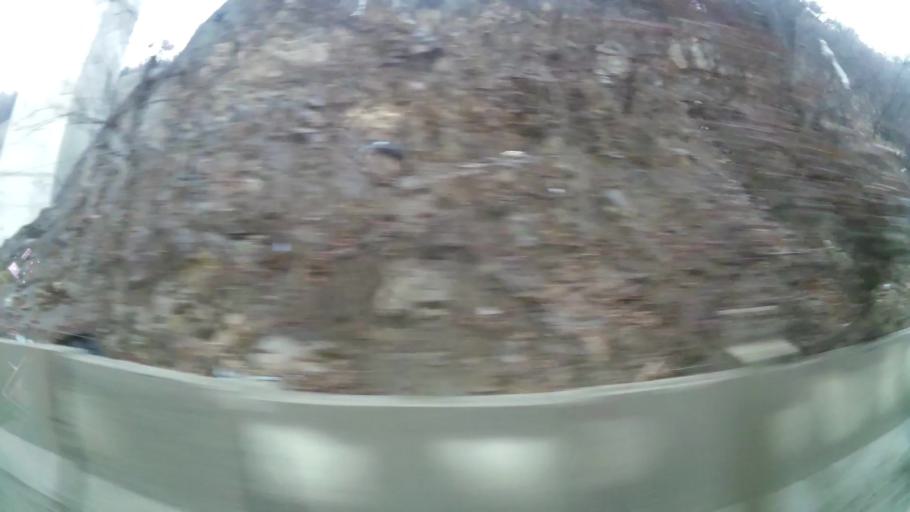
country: XK
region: Ferizaj
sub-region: Hani i Elezit
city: Hani i Elezit
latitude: 42.1697
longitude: 21.2775
